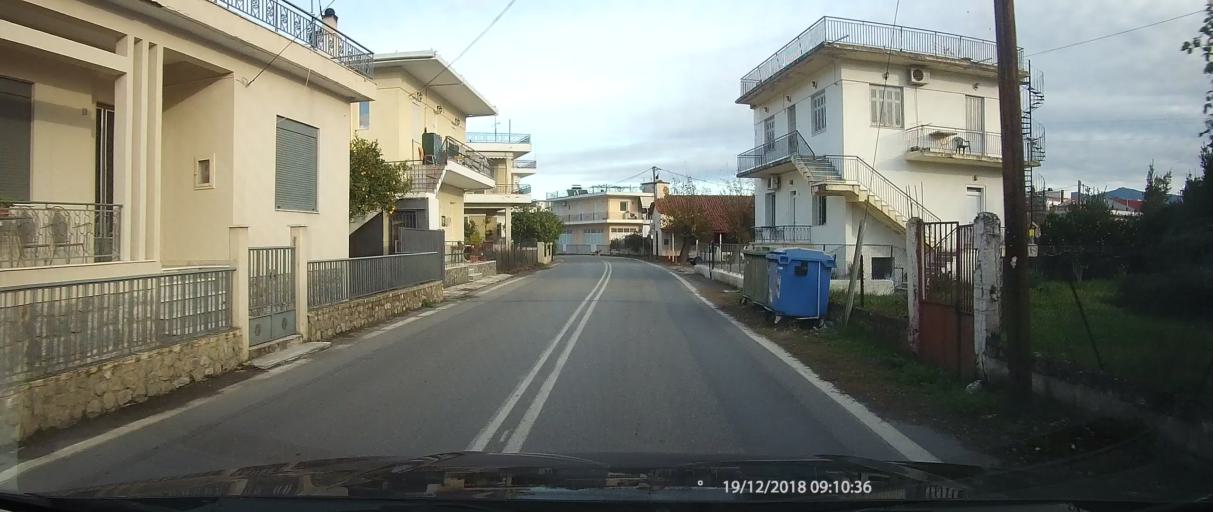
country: GR
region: Peloponnese
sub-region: Nomos Lakonias
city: Sparti
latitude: 37.0756
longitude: 22.4200
